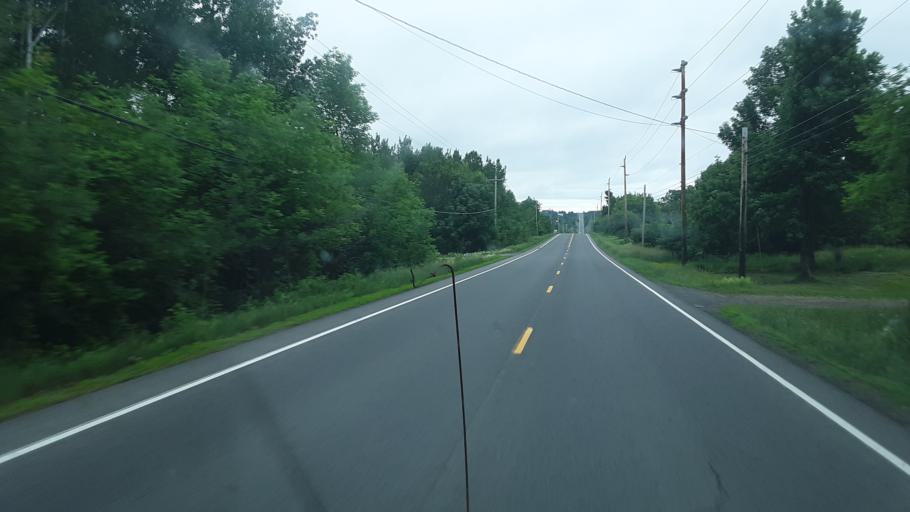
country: US
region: Maine
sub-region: Penobscot County
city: Patten
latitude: 45.9756
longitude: -68.4505
